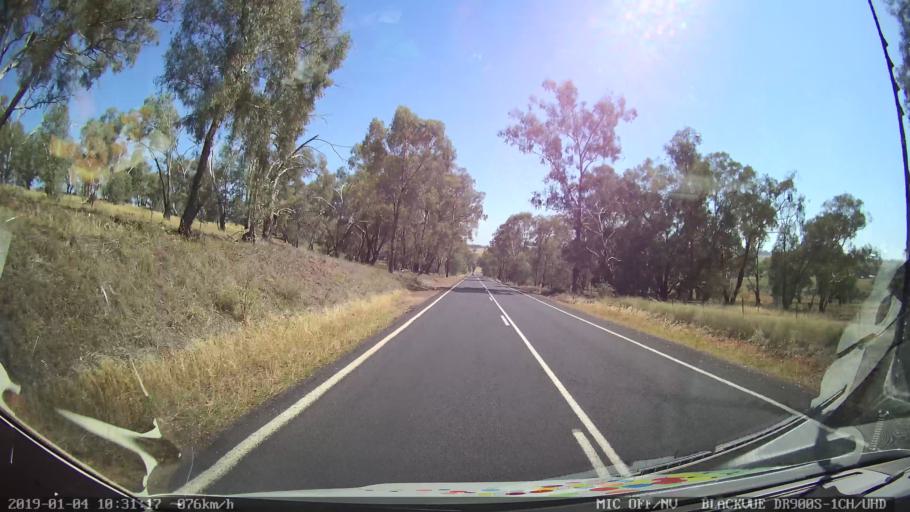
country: AU
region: New South Wales
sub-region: Cabonne
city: Canowindra
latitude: -33.3365
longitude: 148.6319
